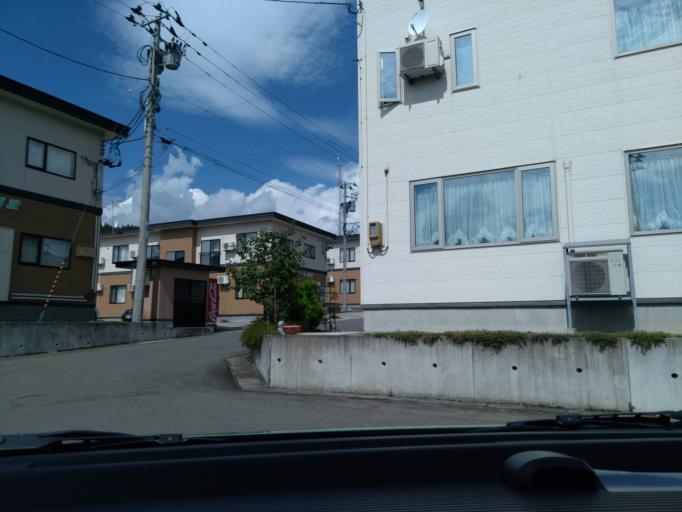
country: JP
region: Akita
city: Kakunodatemachi
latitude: 39.5935
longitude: 140.5731
